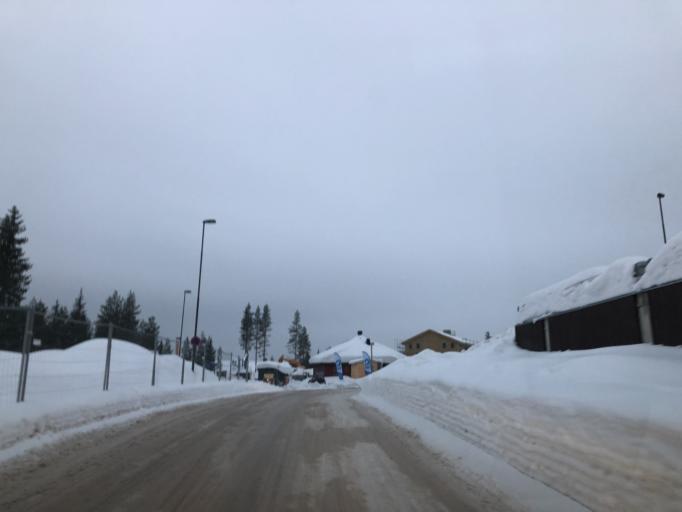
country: NO
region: Hedmark
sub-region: Trysil
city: Innbygda
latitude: 61.3063
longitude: 12.2444
